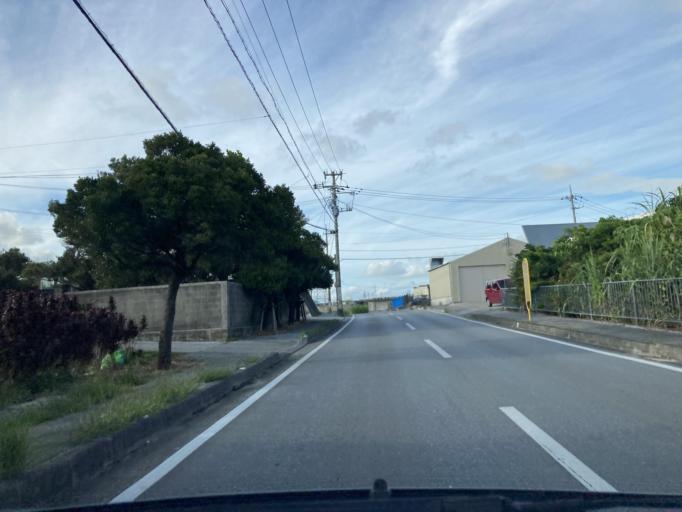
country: JP
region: Okinawa
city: Tomigusuku
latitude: 26.1543
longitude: 127.7414
